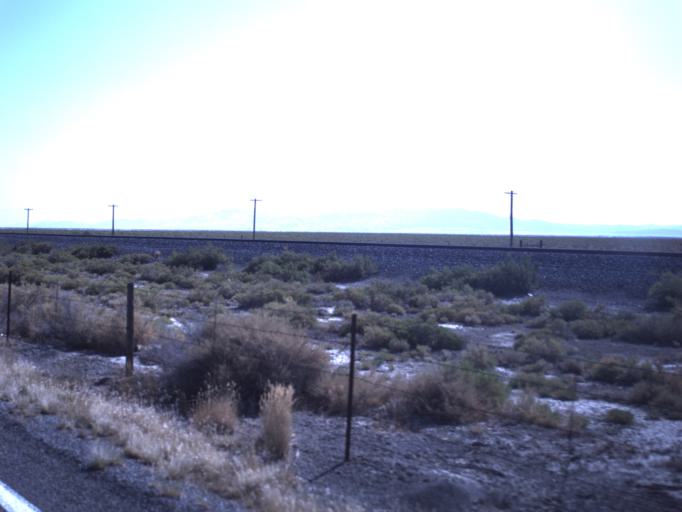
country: US
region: Utah
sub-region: Millard County
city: Delta
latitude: 39.1541
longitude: -112.7167
